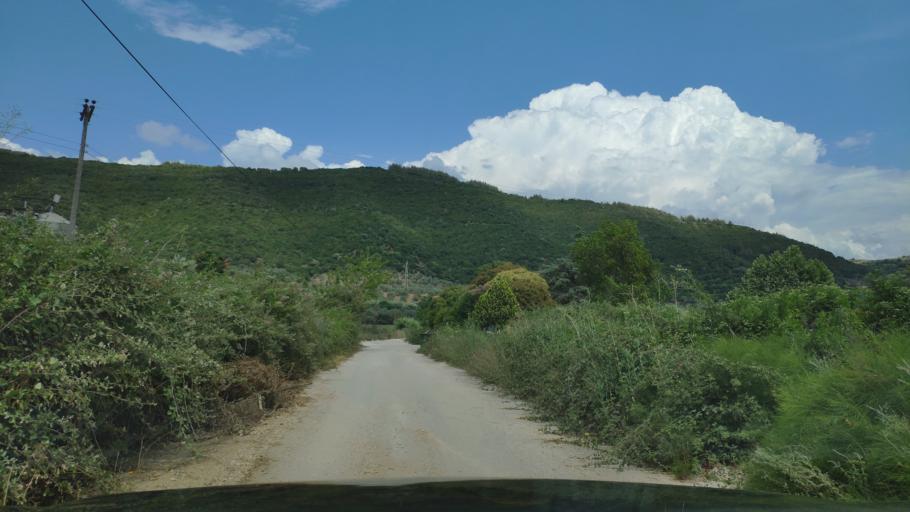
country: GR
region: West Greece
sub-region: Nomos Aitolias kai Akarnanias
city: Menidi
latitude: 39.0625
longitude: 21.0964
